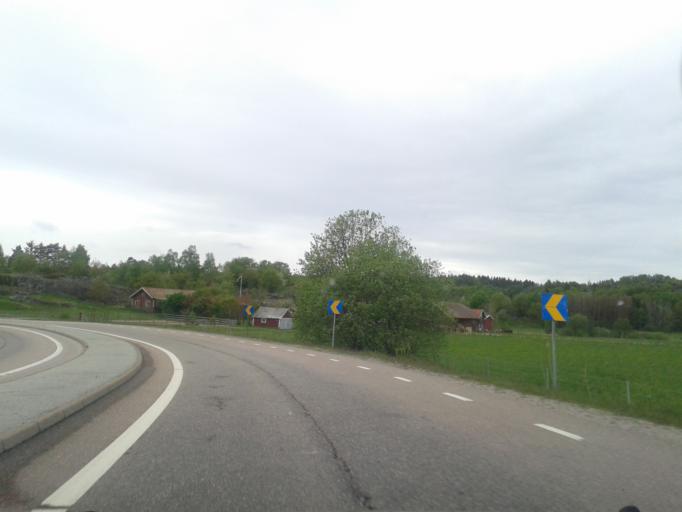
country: SE
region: Vaestra Goetaland
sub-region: Stenungsunds Kommun
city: Stora Hoga
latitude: 58.0261
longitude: 11.8422
